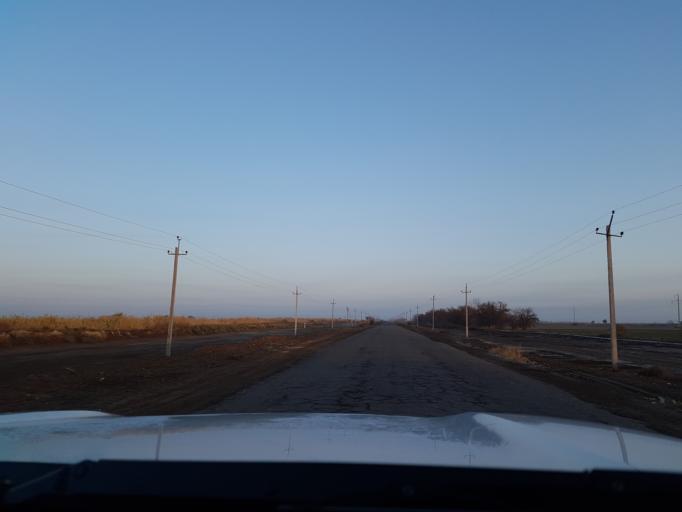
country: TM
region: Dasoguz
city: Koeneuergench
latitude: 41.8356
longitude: 58.7042
